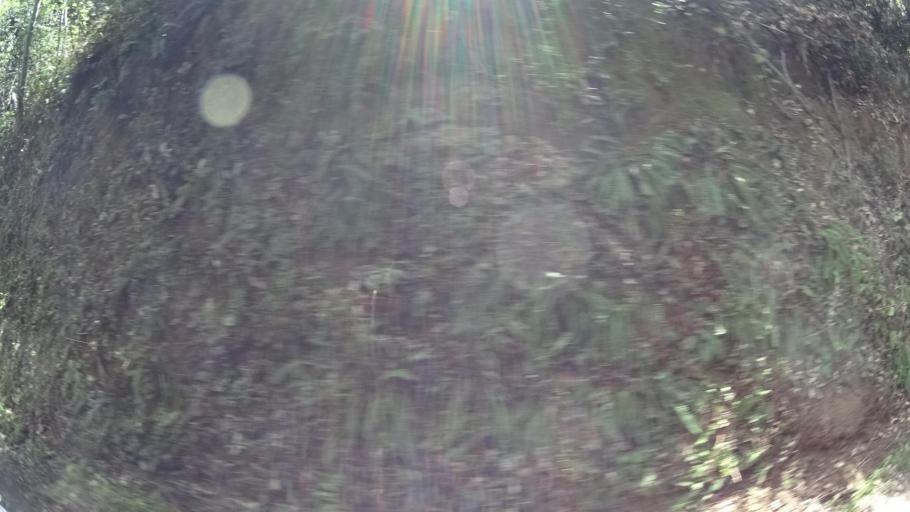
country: US
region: California
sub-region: Humboldt County
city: Blue Lake
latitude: 40.7640
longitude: -123.9466
